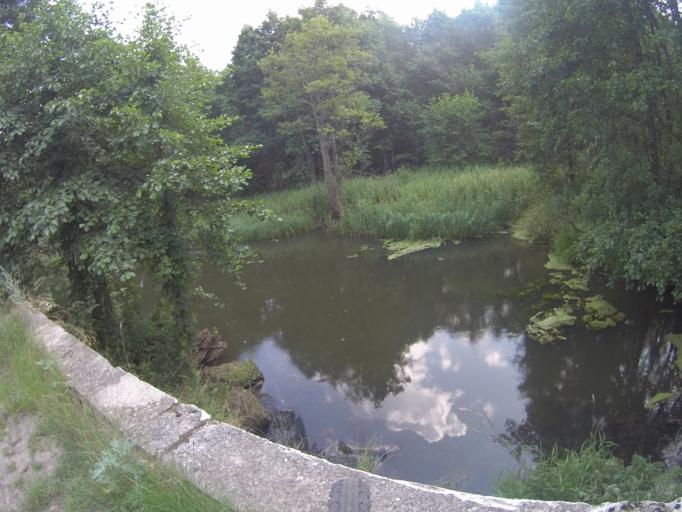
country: RU
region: Vladimir
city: Imeni Vorovskogo
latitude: 55.7377
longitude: 40.9583
